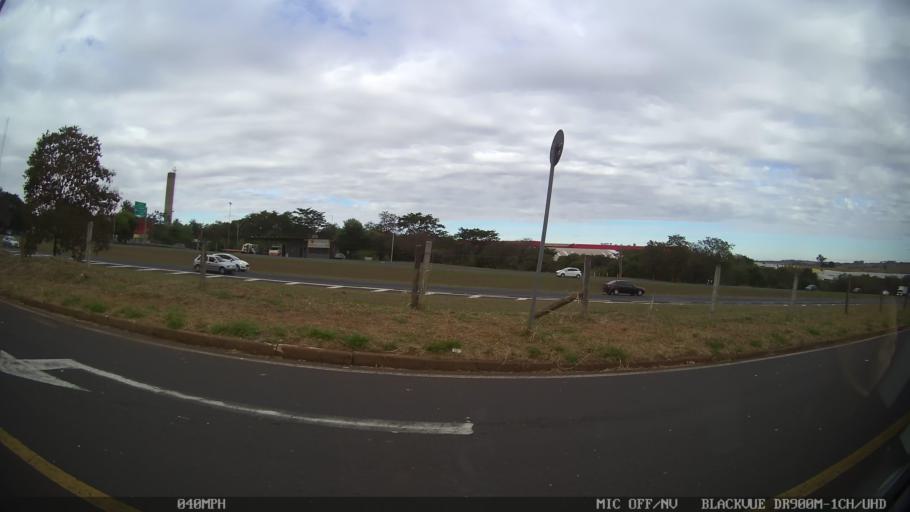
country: BR
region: Sao Paulo
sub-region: Sao Jose Do Rio Preto
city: Sao Jose do Rio Preto
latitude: -20.8217
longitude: -49.4241
